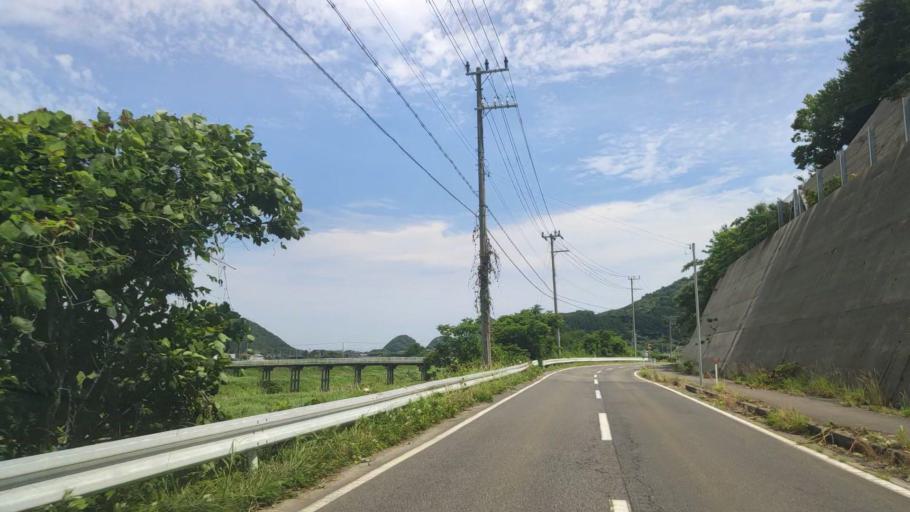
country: JP
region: Hyogo
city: Toyooka
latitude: 35.6448
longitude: 134.7623
